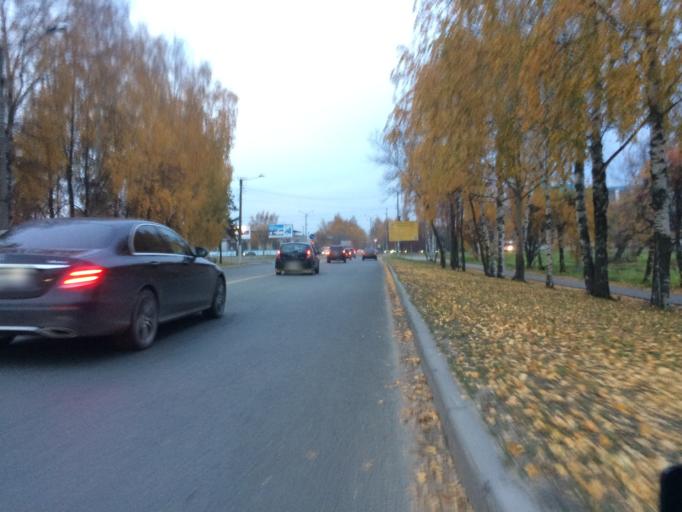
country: RU
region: Mariy-El
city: Yoshkar-Ola
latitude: 56.6088
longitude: 47.8802
